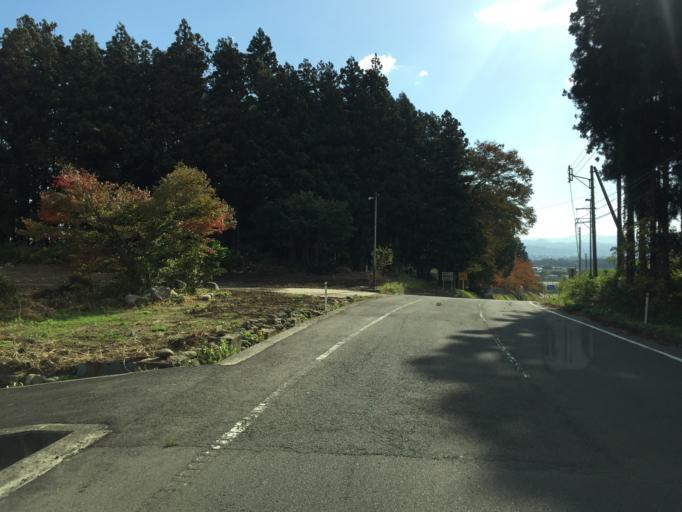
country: JP
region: Fukushima
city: Fukushima-shi
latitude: 37.7963
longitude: 140.3901
